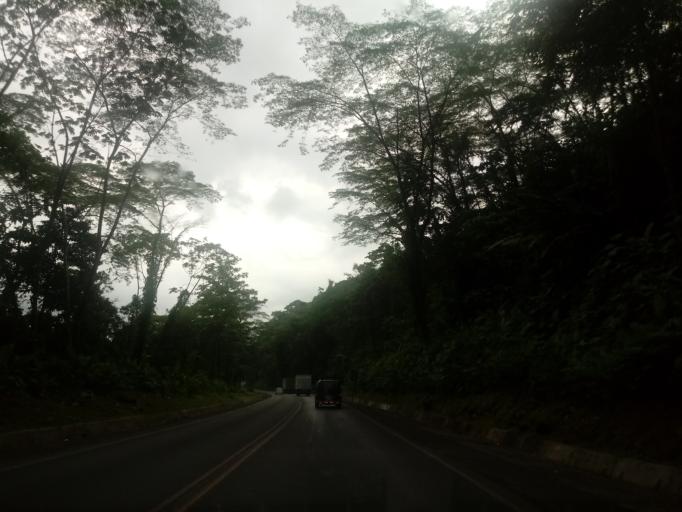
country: CR
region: San Jose
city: Dulce Nombre de Jesus
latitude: 10.1486
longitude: -83.9440
